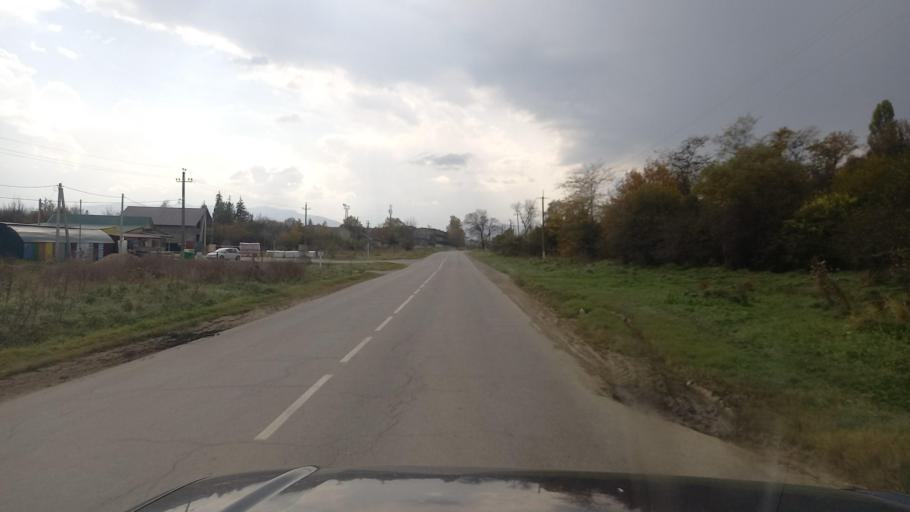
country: RU
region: Krasnodarskiy
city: Psebay
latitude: 44.1423
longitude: 40.8230
